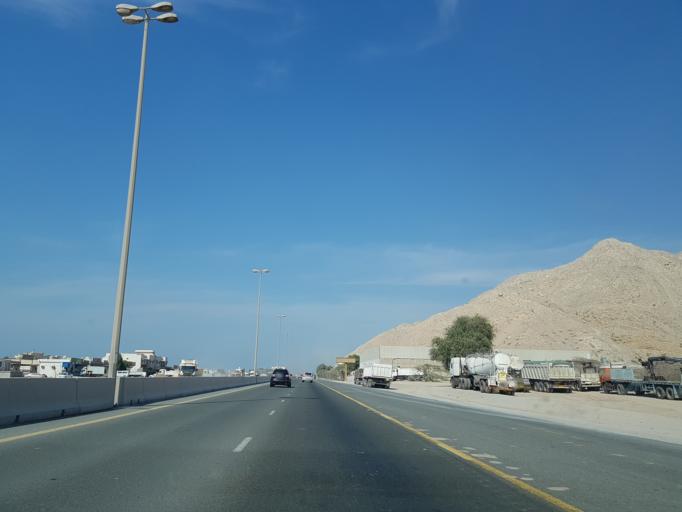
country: AE
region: Ra's al Khaymah
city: Ras al-Khaimah
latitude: 25.8535
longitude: 56.0204
